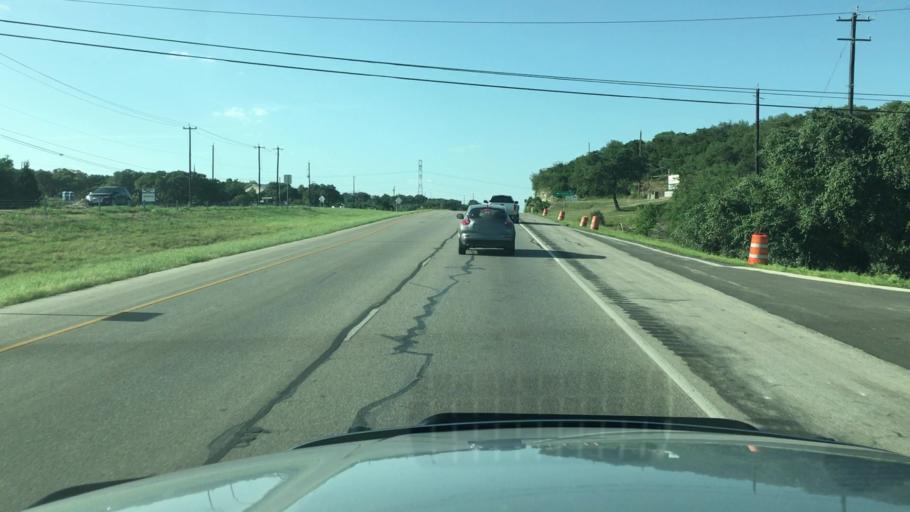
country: US
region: Texas
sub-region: Comal County
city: Bulverde
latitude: 29.7721
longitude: -98.4272
